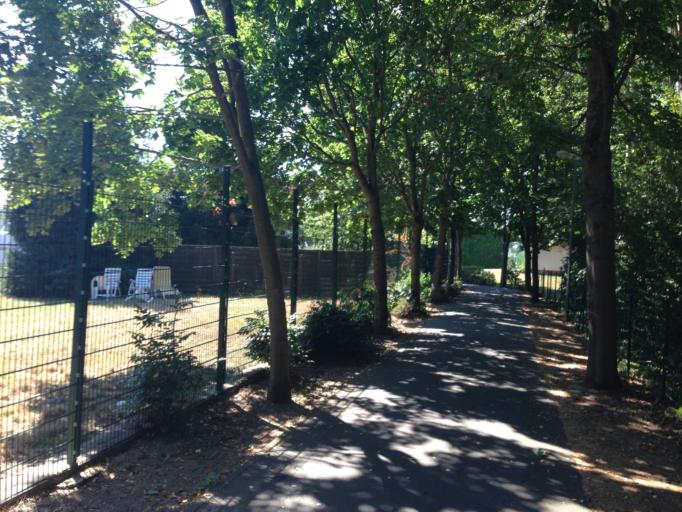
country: DE
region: Hesse
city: Lollar
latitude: 50.6417
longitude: 8.7010
